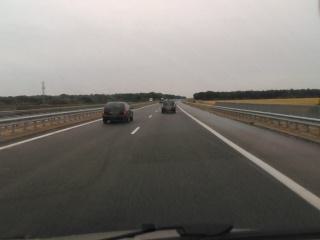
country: BG
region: Stara Zagora
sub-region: Obshtina Stara Zagora
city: Stara Zagora
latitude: 42.3599
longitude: 25.7557
